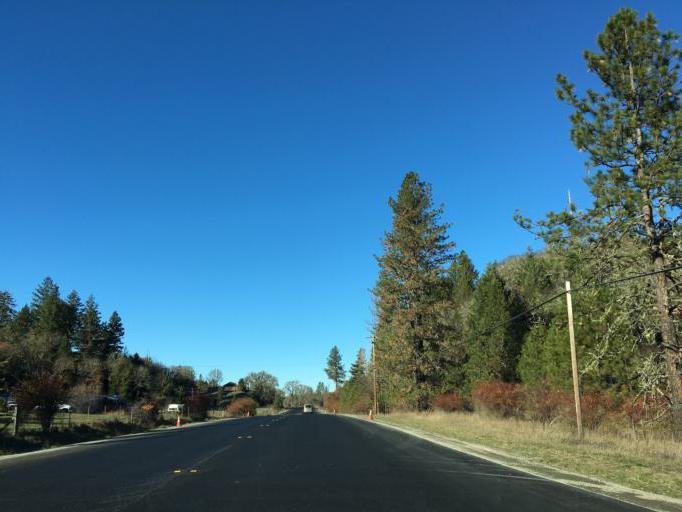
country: US
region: California
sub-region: Mendocino County
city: Laytonville
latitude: 39.6368
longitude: -123.4694
